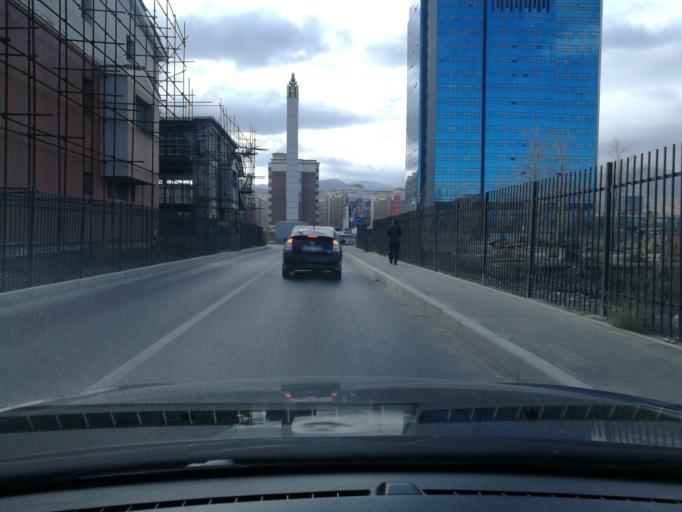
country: MN
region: Ulaanbaatar
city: Ulaanbaatar
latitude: 47.9051
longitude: 106.9184
